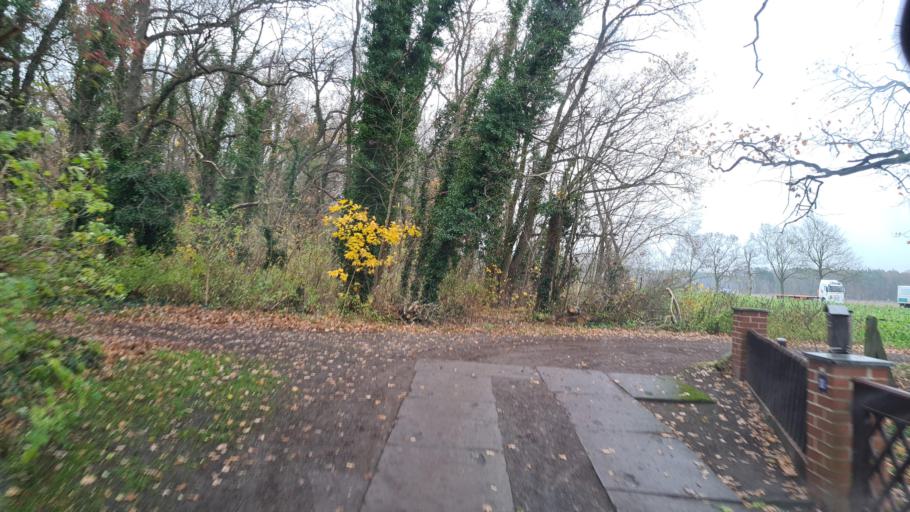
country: DE
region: Brandenburg
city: Retzow
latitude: 52.6320
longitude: 12.7230
